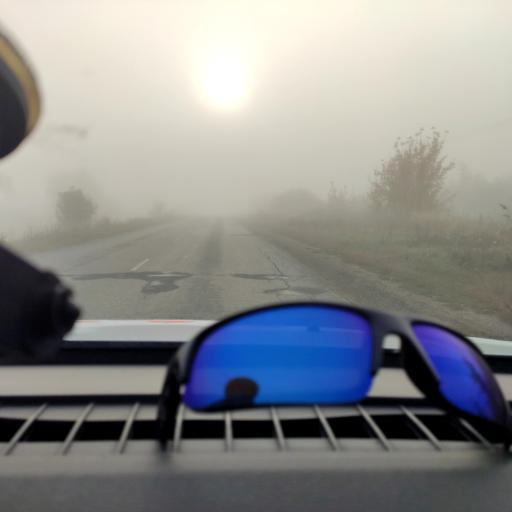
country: RU
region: Samara
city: Chapayevsk
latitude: 53.0049
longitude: 49.7456
